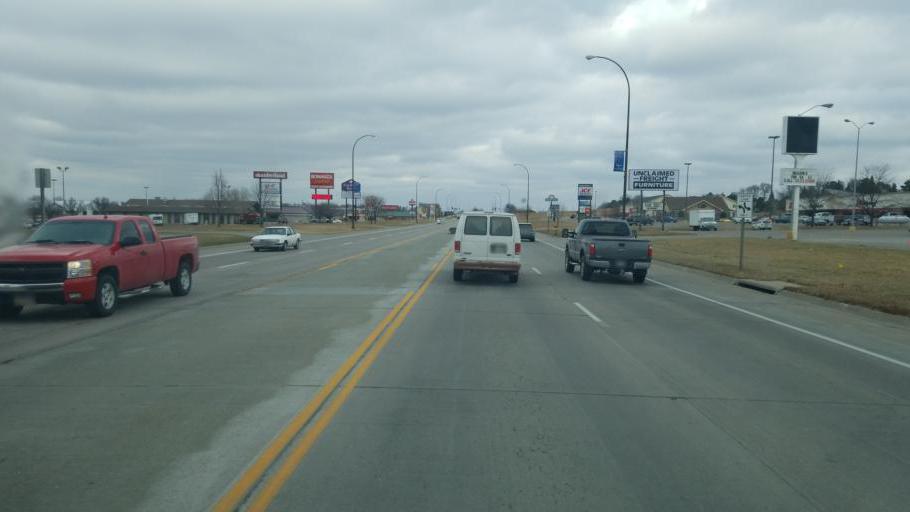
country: US
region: South Dakota
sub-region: Yankton County
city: Yankton
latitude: 42.8947
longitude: -97.3974
